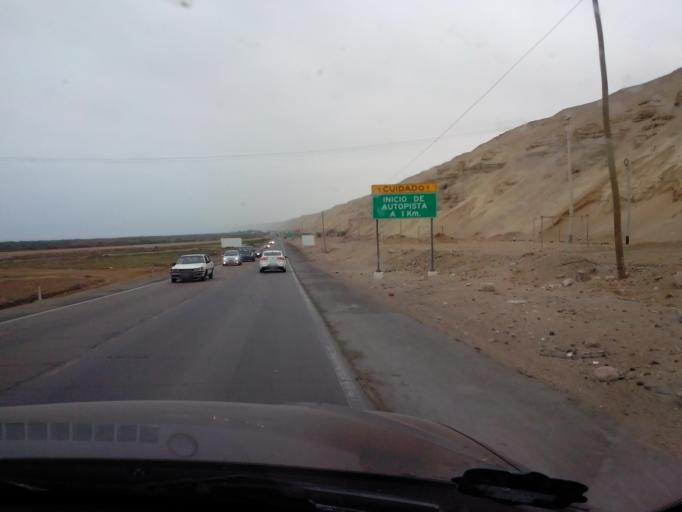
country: PE
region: Ica
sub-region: Provincia de Chincha
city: Sunampe
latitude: -13.4108
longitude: -76.1902
